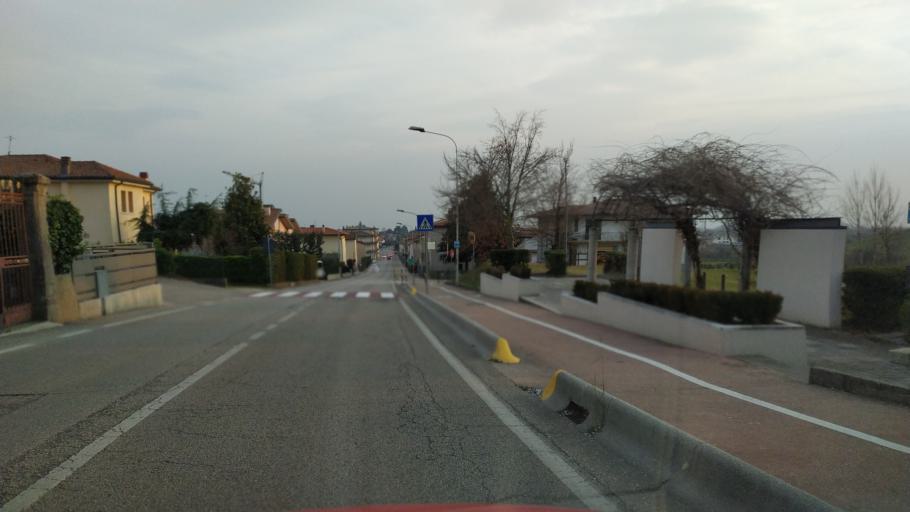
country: IT
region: Veneto
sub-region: Provincia di Vicenza
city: Sarcedo
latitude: 45.7041
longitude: 11.5305
